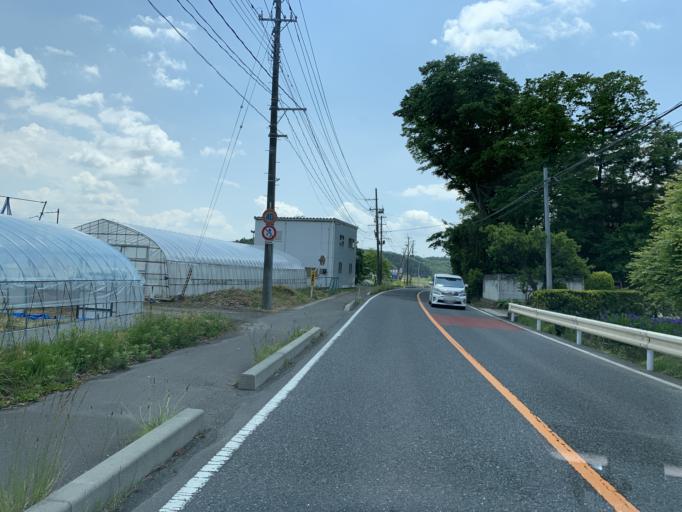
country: JP
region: Miyagi
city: Kogota
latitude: 38.5019
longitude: 141.0803
